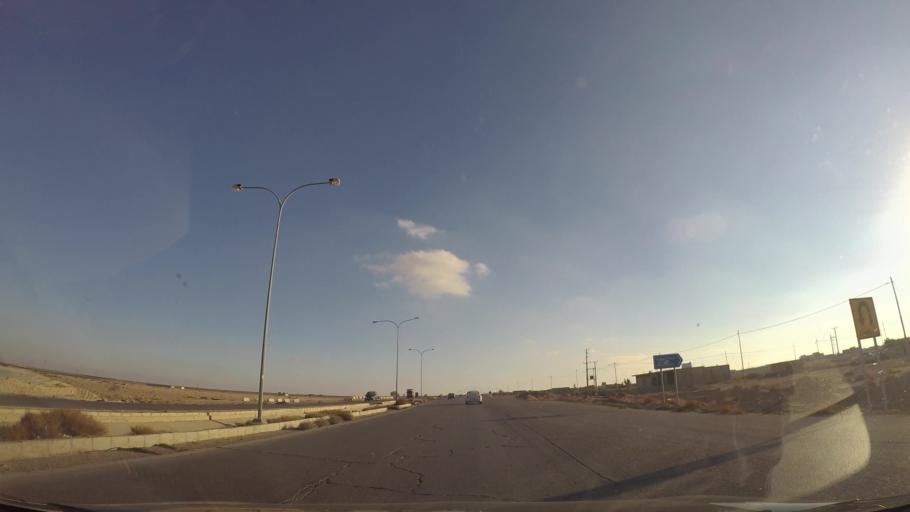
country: JO
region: Tafielah
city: Busayra
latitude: 30.5748
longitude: 35.7987
